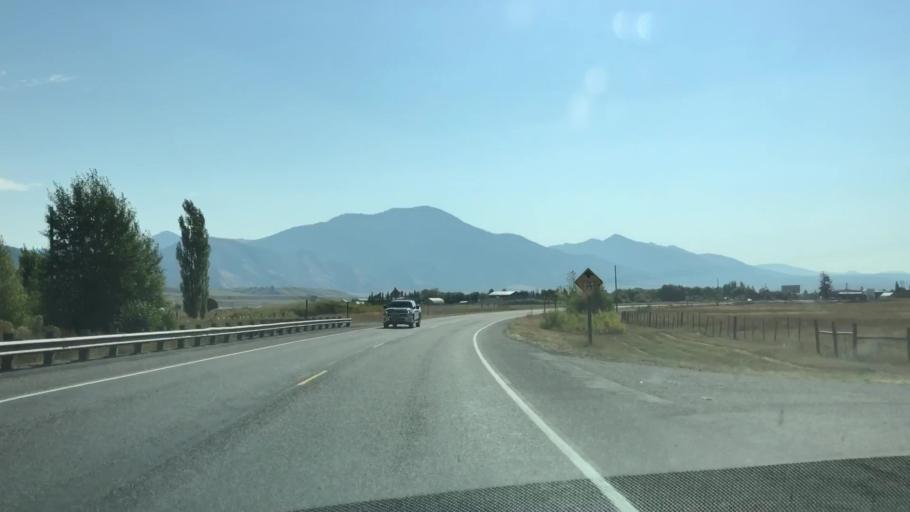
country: US
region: Idaho
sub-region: Teton County
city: Victor
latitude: 43.4557
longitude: -111.3462
